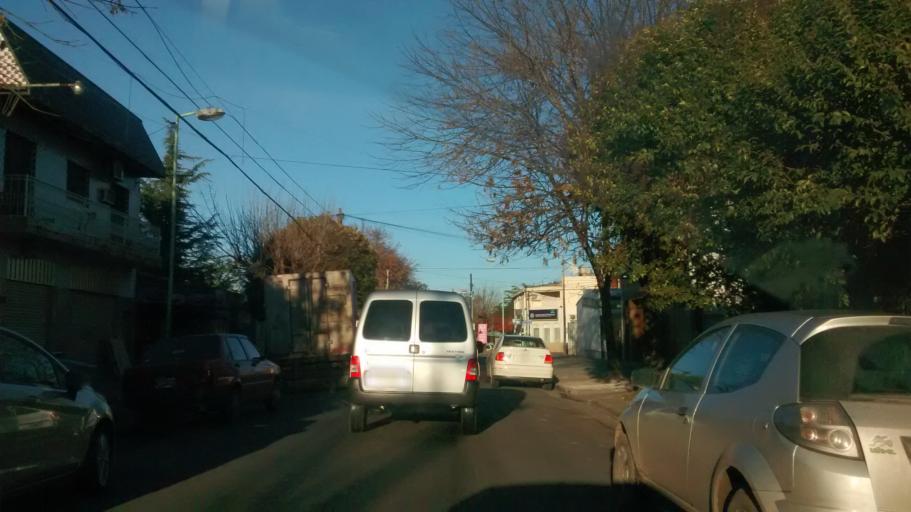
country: AR
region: Buenos Aires
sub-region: Partido de La Plata
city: La Plata
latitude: -34.9493
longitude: -57.9625
